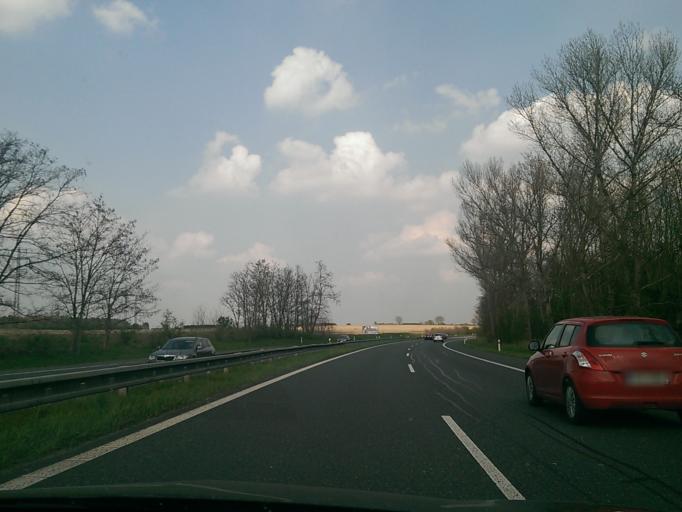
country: CZ
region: Central Bohemia
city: Benatky nad Jizerou
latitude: 50.2593
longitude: 14.7756
